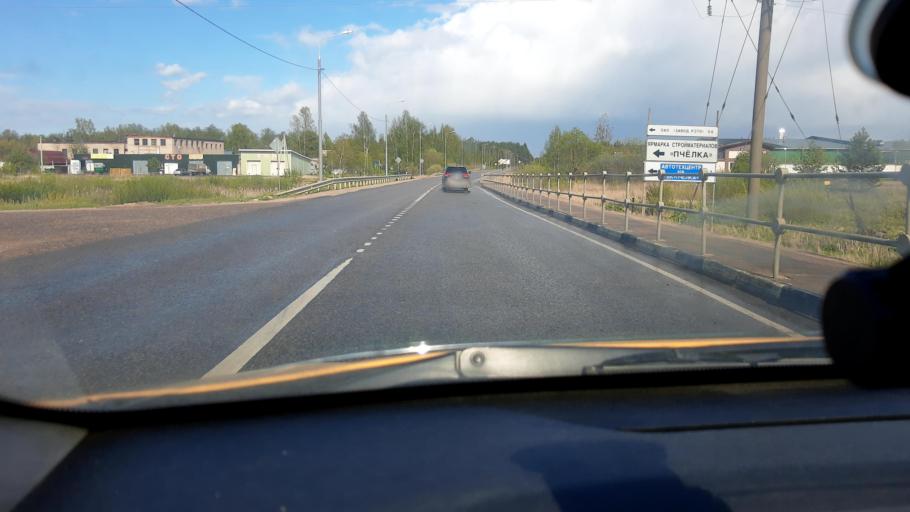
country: RU
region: Moskovskaya
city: Ruza
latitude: 55.7061
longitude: 36.2152
